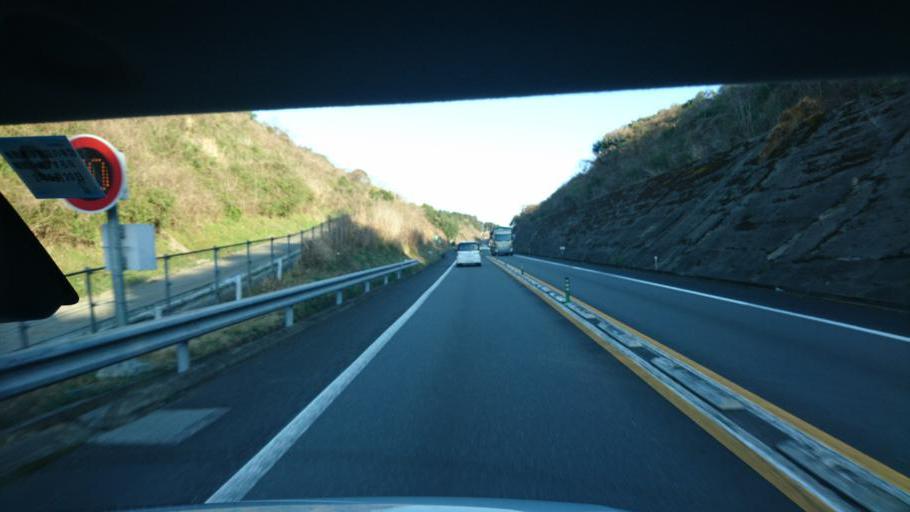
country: JP
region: Miyazaki
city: Miyazaki-shi
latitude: 31.8932
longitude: 131.3672
